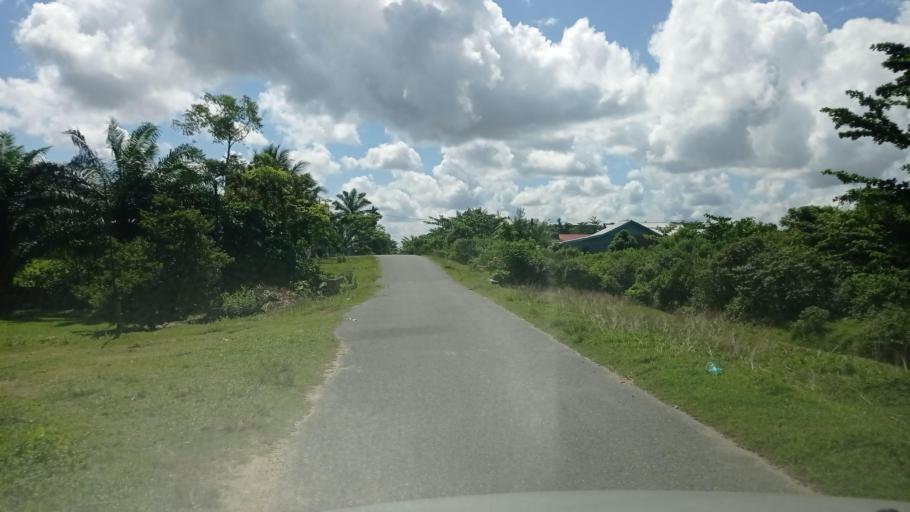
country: ID
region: Jambi
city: Sungai Penuh
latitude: -2.5508
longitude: 101.1025
